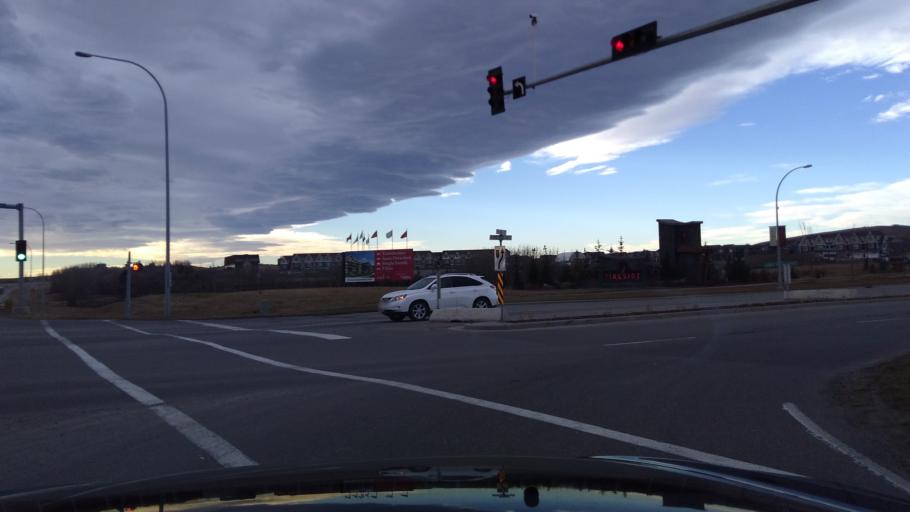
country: CA
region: Alberta
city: Cochrane
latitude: 51.1590
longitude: -114.4703
